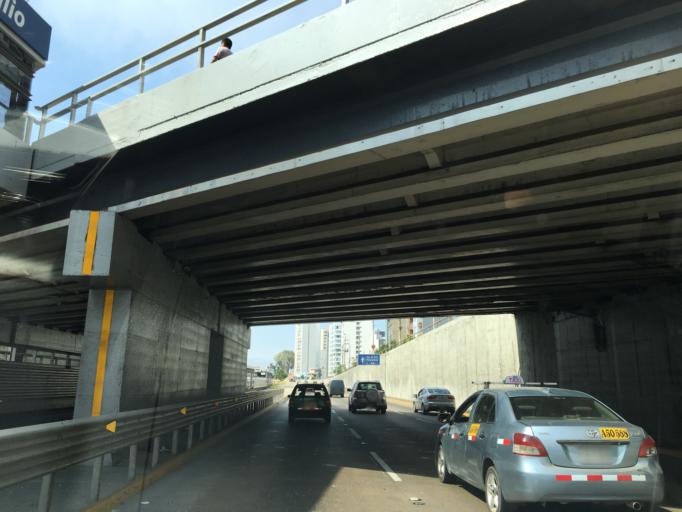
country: PE
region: Lima
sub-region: Lima
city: Surco
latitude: -12.1294
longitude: -77.0229
